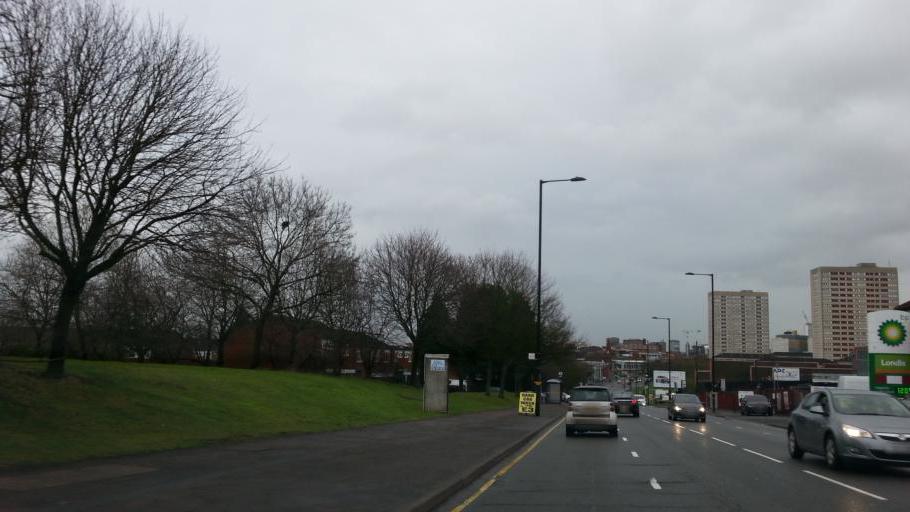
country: GB
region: England
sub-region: City and Borough of Birmingham
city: Hockley
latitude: 52.4866
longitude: -1.9270
